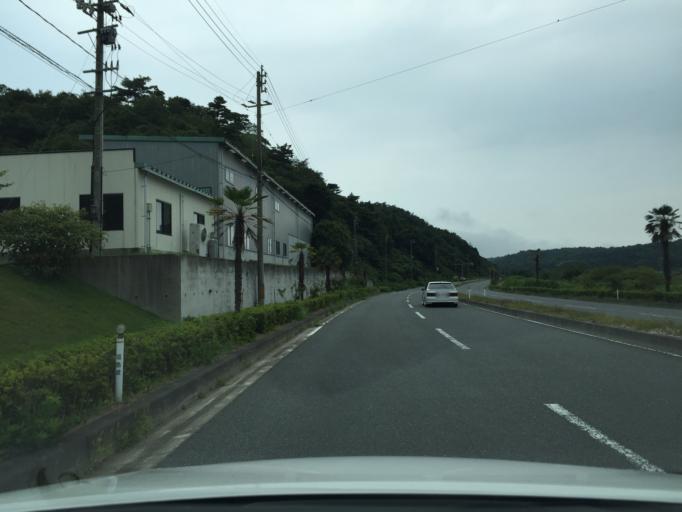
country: JP
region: Fukushima
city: Iwaki
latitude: 36.9633
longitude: 140.9197
